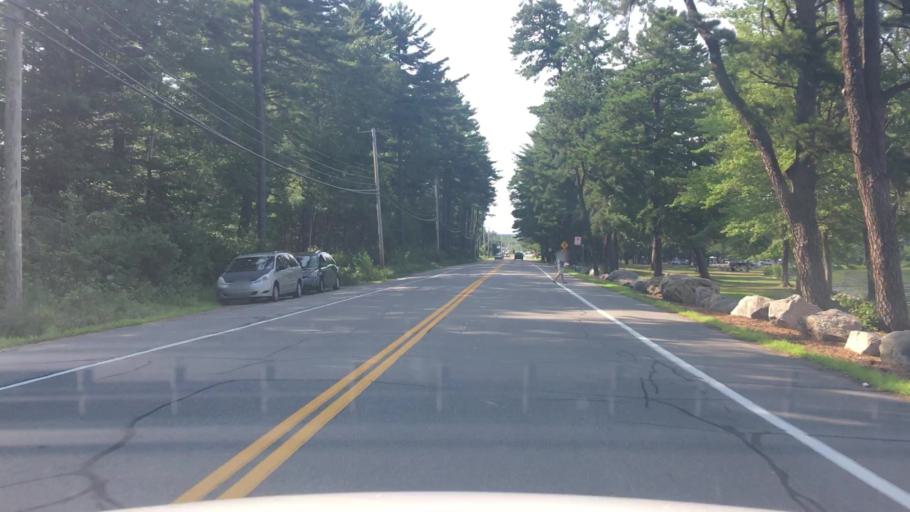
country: US
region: New Hampshire
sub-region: Rockingham County
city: Auburn
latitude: 43.0001
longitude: -71.3888
